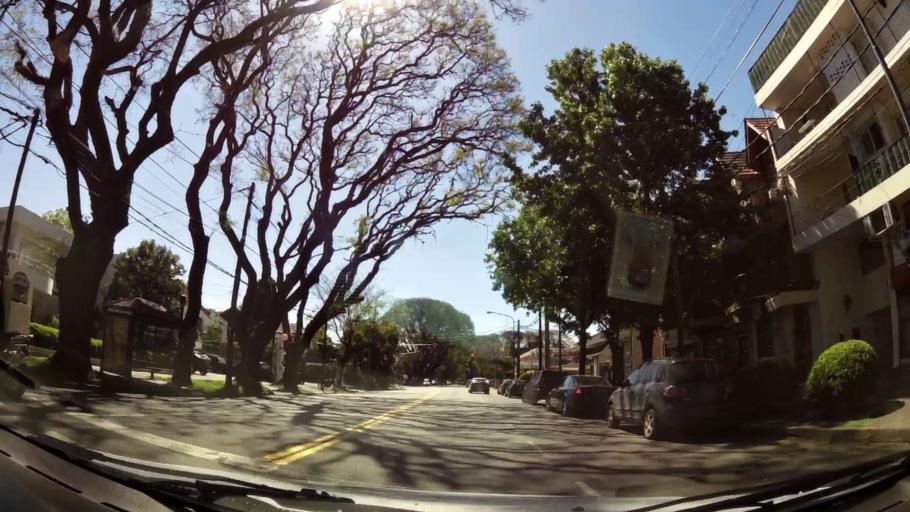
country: AR
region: Buenos Aires
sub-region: Partido de San Isidro
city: San Isidro
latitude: -34.4746
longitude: -58.5016
